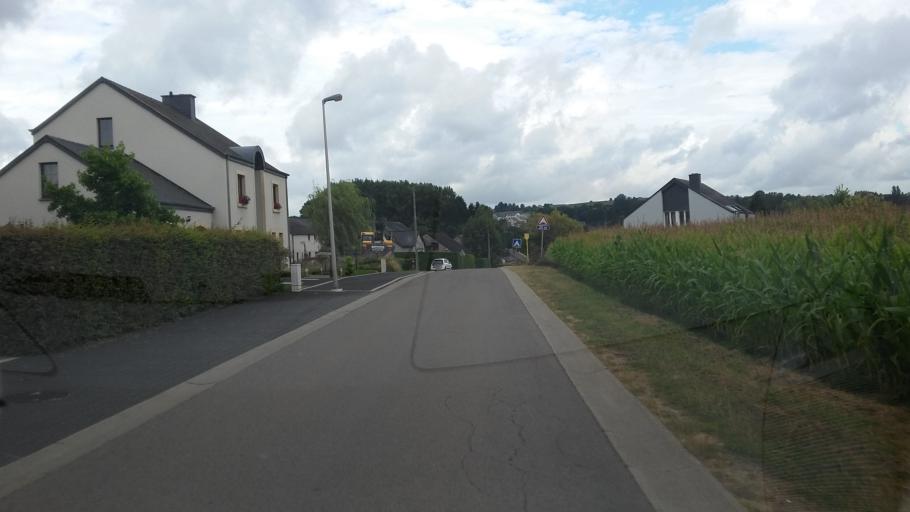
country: BE
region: Wallonia
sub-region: Province du Luxembourg
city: Arlon
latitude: 49.6773
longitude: 5.8454
